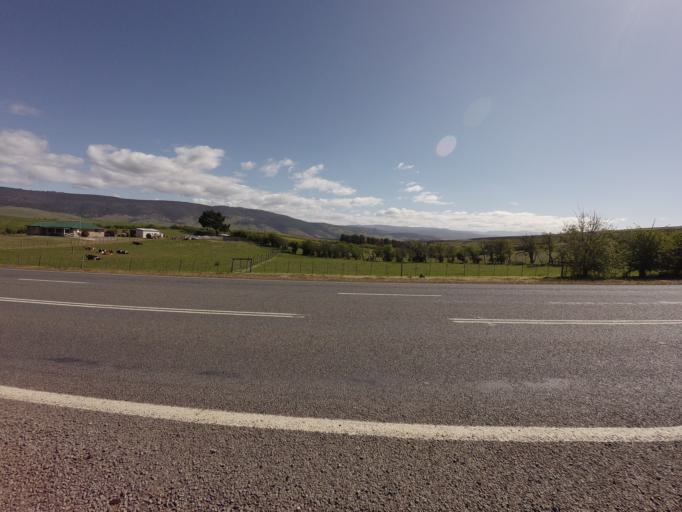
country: AU
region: Tasmania
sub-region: Derwent Valley
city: New Norfolk
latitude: -42.7177
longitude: 146.9482
